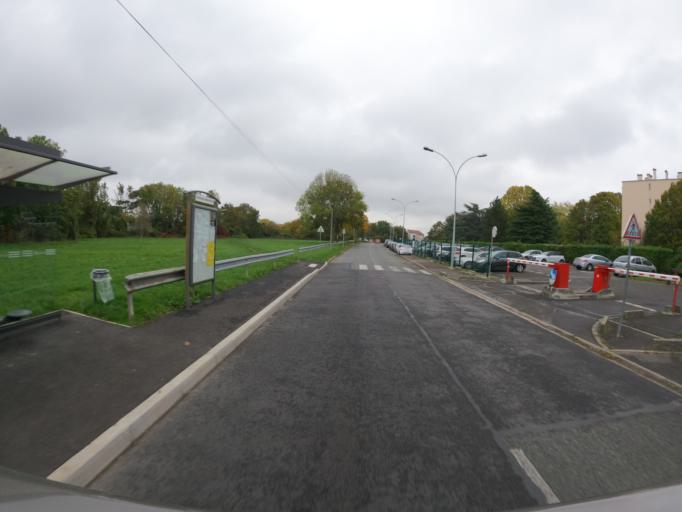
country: FR
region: Ile-de-France
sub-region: Departement du Val-de-Marne
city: Chennevieres-sur-Marne
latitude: 48.7899
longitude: 2.5293
